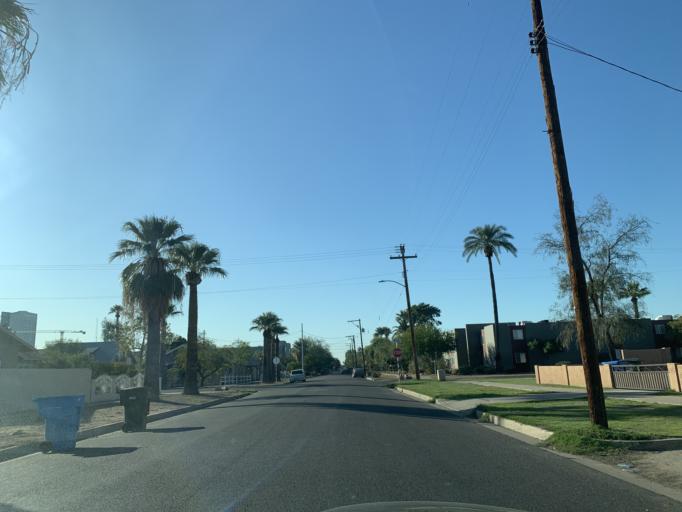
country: US
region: Arizona
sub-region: Maricopa County
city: Phoenix
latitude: 33.4599
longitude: -112.0615
